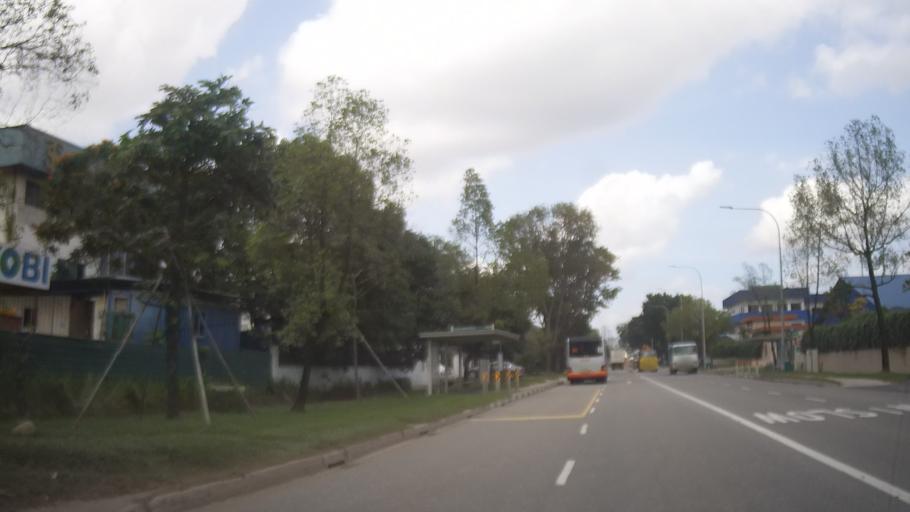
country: MY
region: Johor
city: Johor Bahru
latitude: 1.4316
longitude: 103.7474
